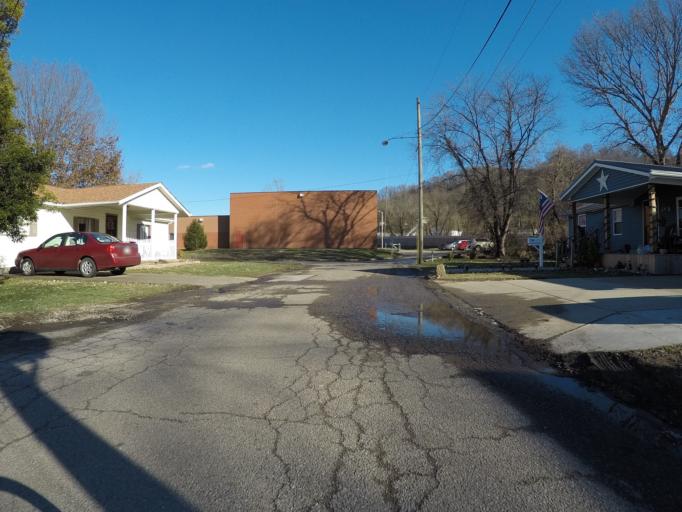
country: US
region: West Virginia
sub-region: Cabell County
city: Huntington
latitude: 38.4262
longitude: -82.3855
